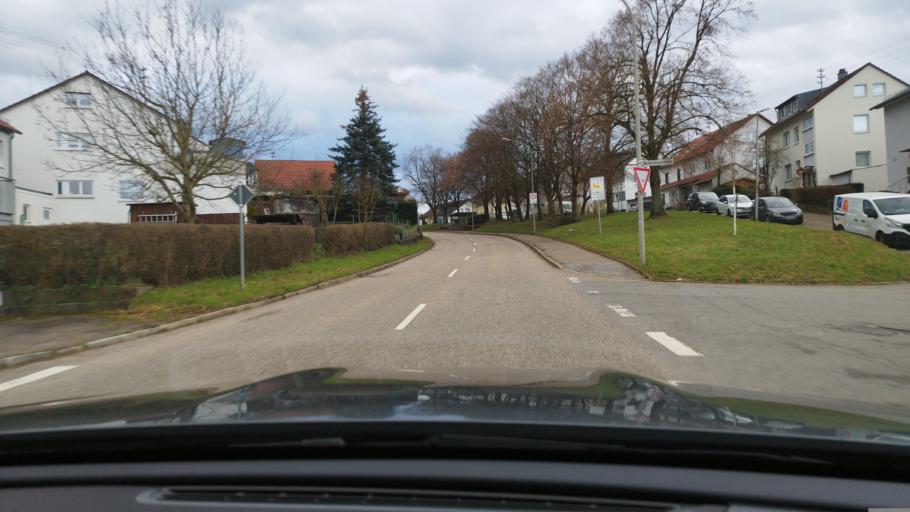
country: DE
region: Baden-Wuerttemberg
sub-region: Regierungsbezirk Stuttgart
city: Leutenbach
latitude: 48.8912
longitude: 9.3858
